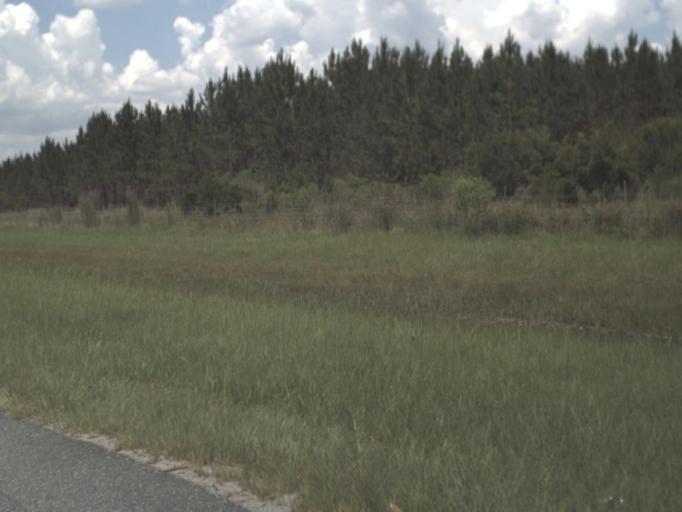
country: US
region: Florida
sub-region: Bradford County
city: Starke
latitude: 30.0095
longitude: -82.0525
